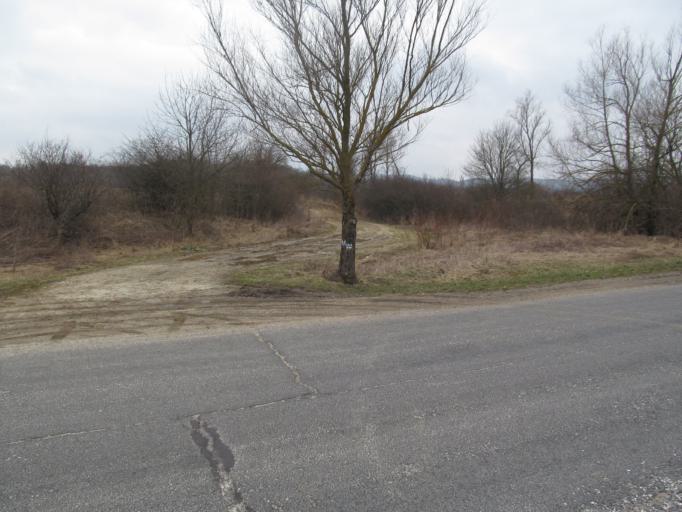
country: HU
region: Veszprem
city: Urkut
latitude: 47.1594
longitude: 17.6711
